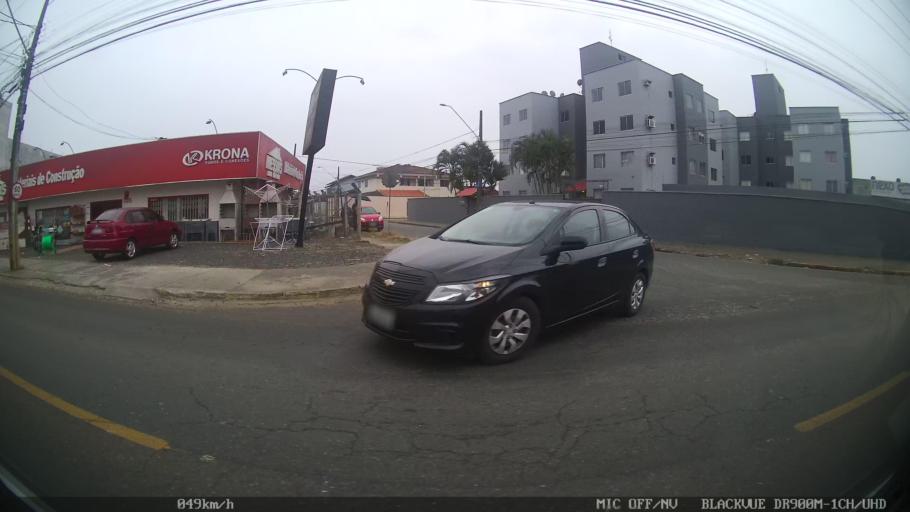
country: BR
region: Santa Catarina
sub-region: Joinville
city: Joinville
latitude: -26.2834
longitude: -48.8016
